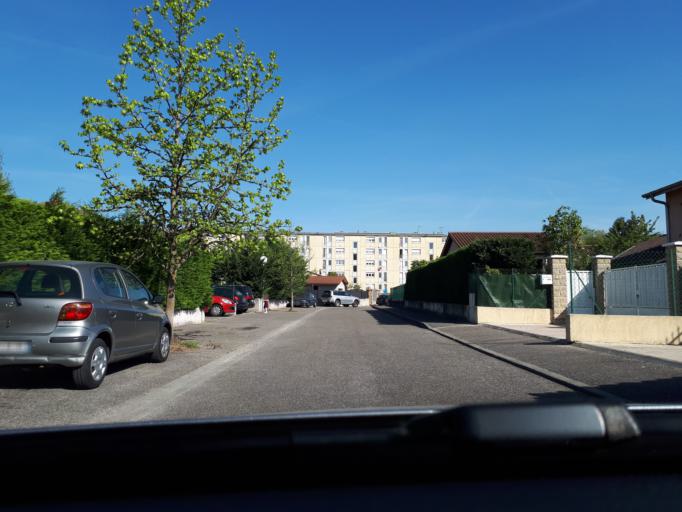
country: FR
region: Rhone-Alpes
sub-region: Departement de l'Isere
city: Bourgoin-Jallieu
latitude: 45.6022
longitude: 5.2680
